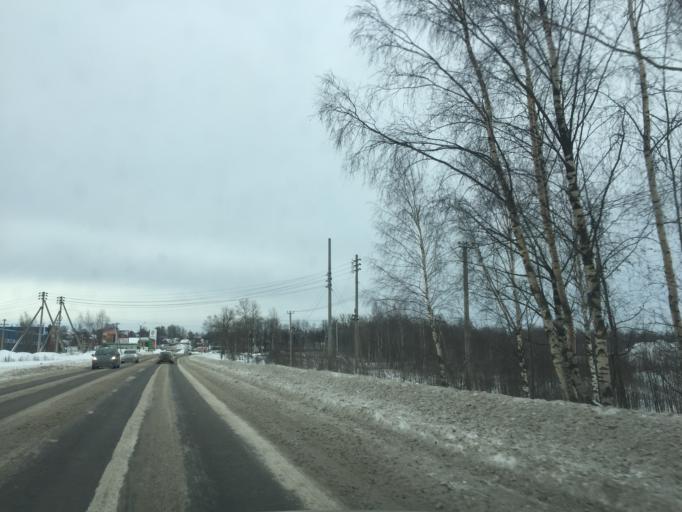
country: RU
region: Leningrad
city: Yanino Vtoroye
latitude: 59.9442
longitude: 30.6002
